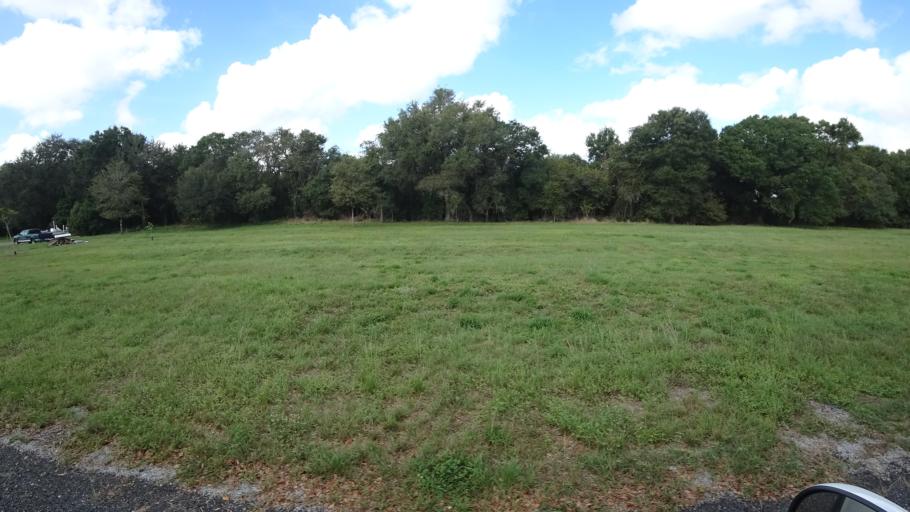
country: US
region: Florida
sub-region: Sarasota County
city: The Meadows
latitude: 27.4750
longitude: -82.2866
